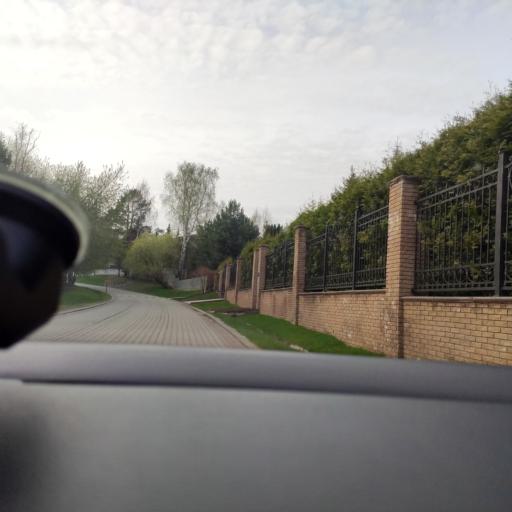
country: RU
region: Moskovskaya
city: Zhavoronki
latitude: 55.6886
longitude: 37.0959
